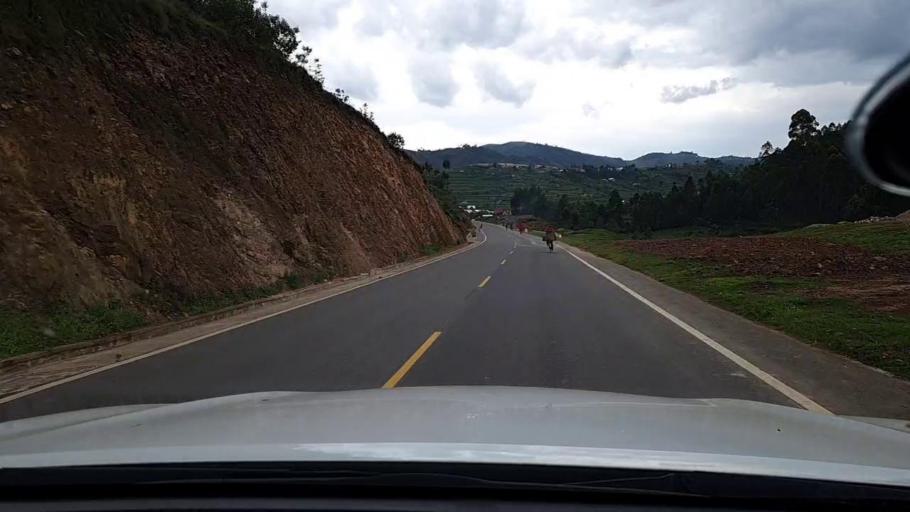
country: RW
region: Northern Province
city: Byumba
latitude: -1.6399
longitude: 29.9264
